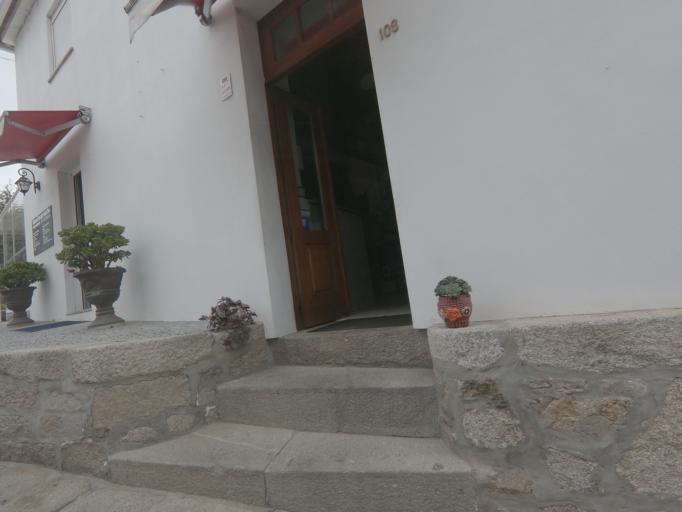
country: PT
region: Viana do Castelo
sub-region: Vila Nova de Cerveira
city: Vila Nova de Cerveira
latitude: 41.9418
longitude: -8.7418
